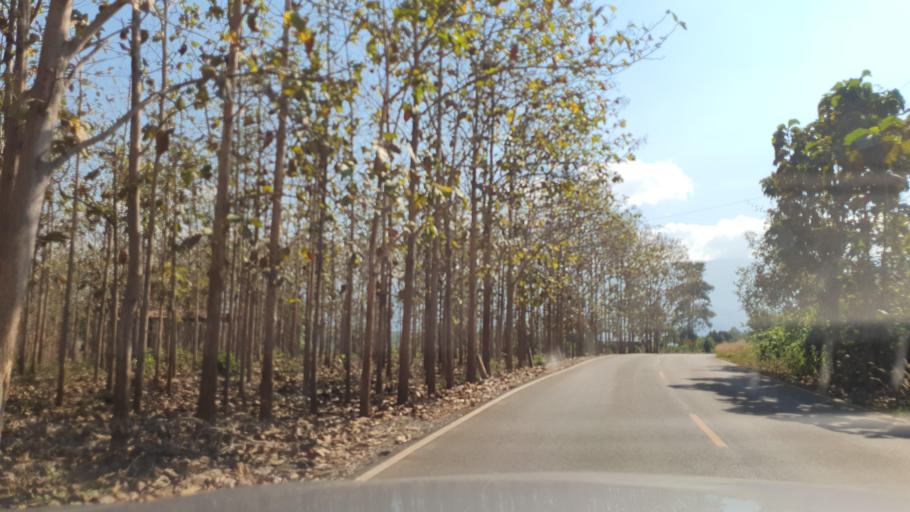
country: TH
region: Nan
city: Pua
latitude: 19.1505
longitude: 100.9141
